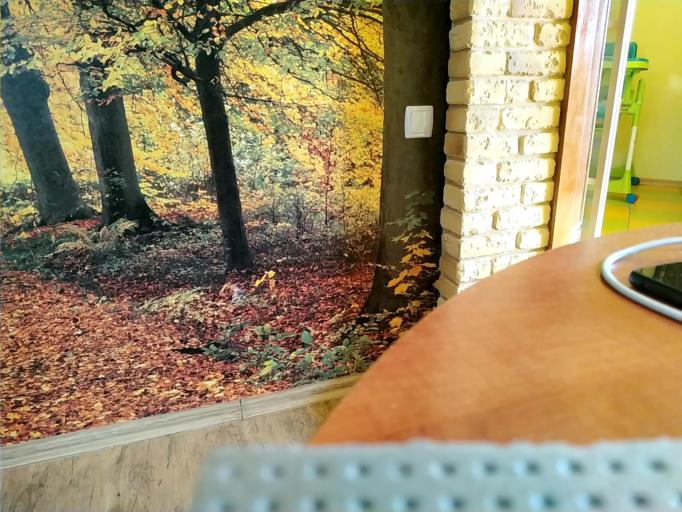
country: RU
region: Tverskaya
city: Kalashnikovo
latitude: 57.3485
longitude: 35.2011
